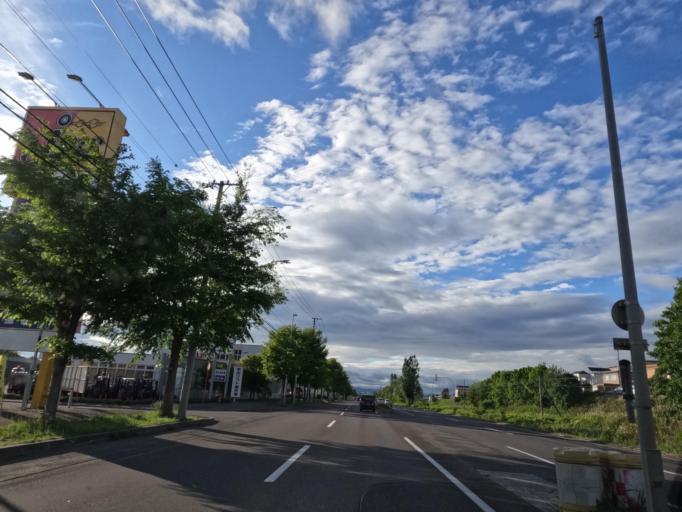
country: JP
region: Hokkaido
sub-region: Asahikawa-shi
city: Asahikawa
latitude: 43.7317
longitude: 142.3647
